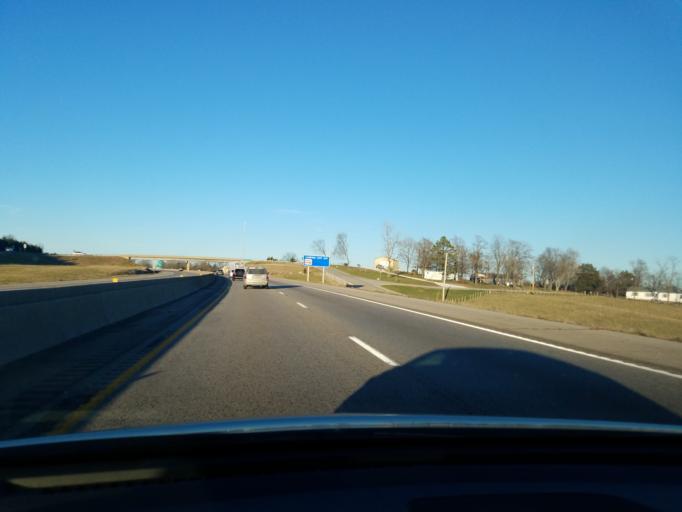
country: US
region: Missouri
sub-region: Franklin County
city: Villa Ridge
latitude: 38.4246
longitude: -90.9163
